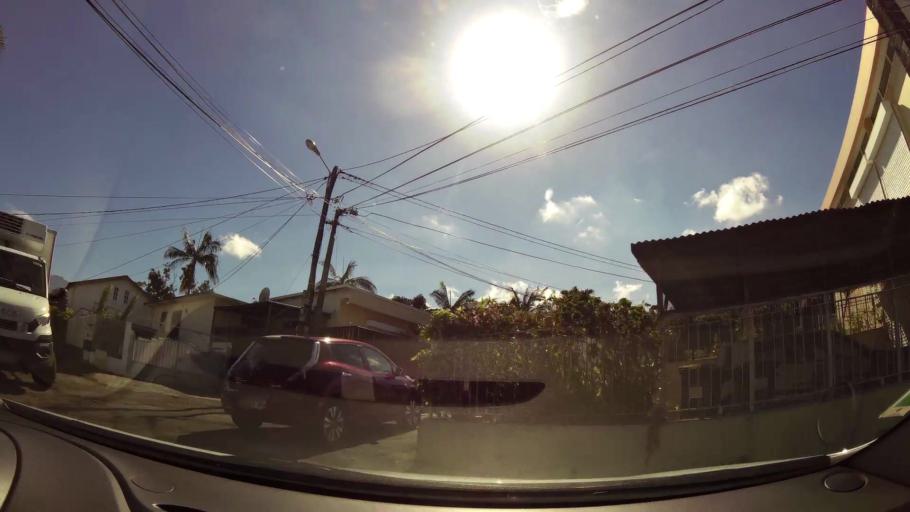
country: RE
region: Reunion
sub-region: Reunion
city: Le Tampon
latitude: -21.2633
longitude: 55.5048
